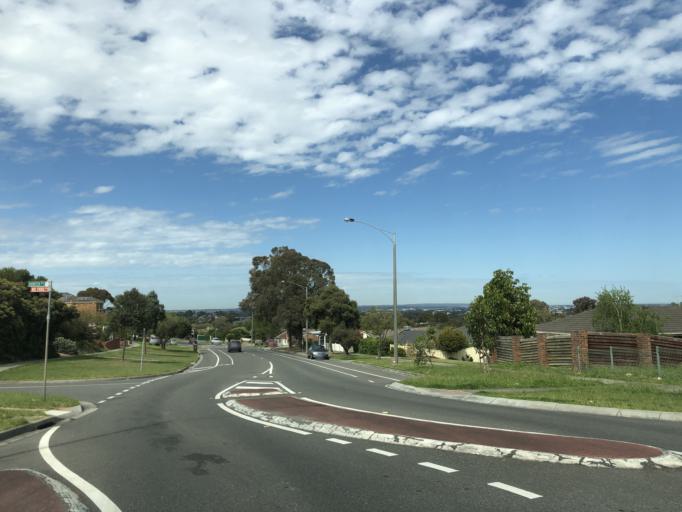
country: AU
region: Victoria
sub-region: Casey
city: Endeavour Hills
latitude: -37.9825
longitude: 145.2554
